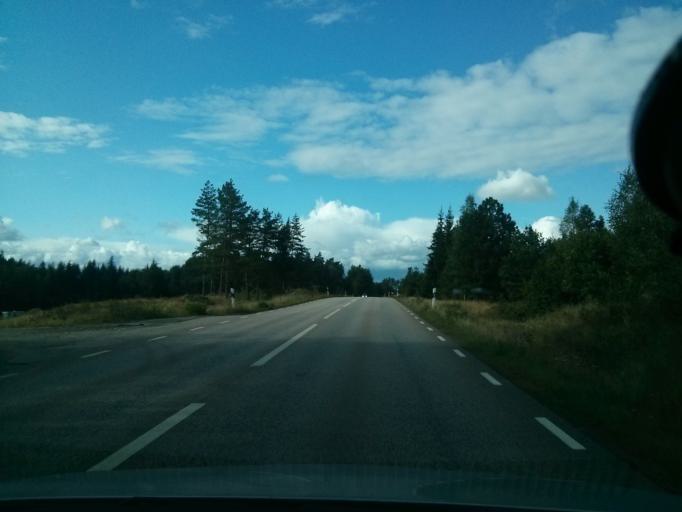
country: SE
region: Blekinge
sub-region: Ronneby Kommun
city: Brakne-Hoby
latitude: 56.3179
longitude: 15.1759
